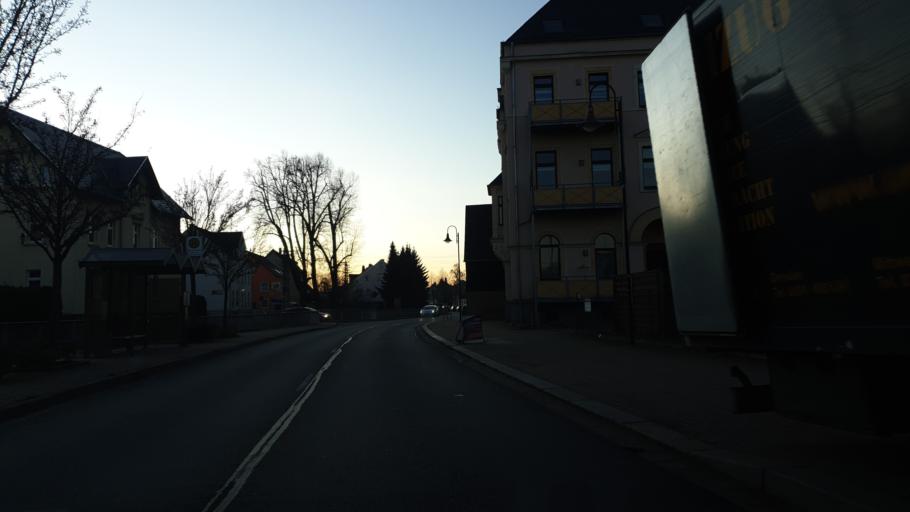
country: DE
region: Saxony
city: Oberlungwitz
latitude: 50.7832
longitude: 12.7088
